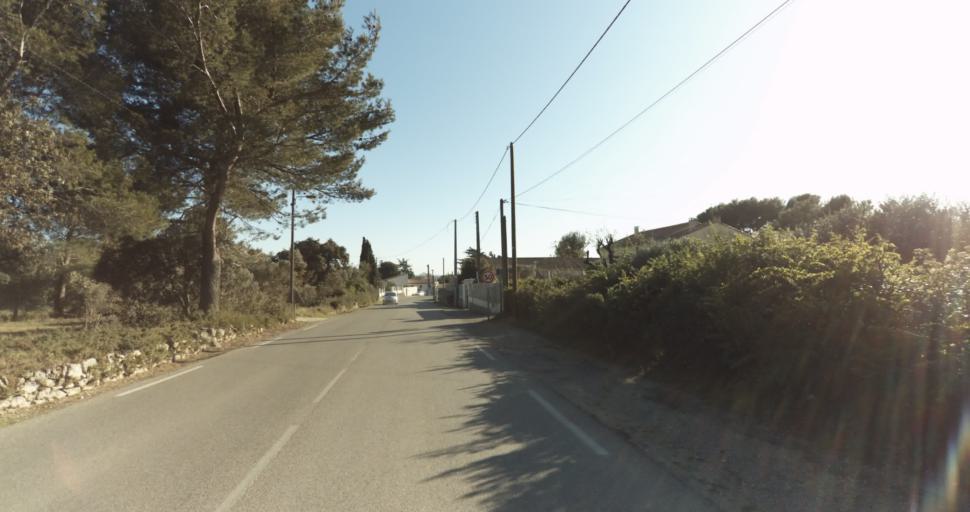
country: FR
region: Provence-Alpes-Cote d'Azur
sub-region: Departement des Bouches-du-Rhone
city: Pelissanne
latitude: 43.6405
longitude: 5.1542
